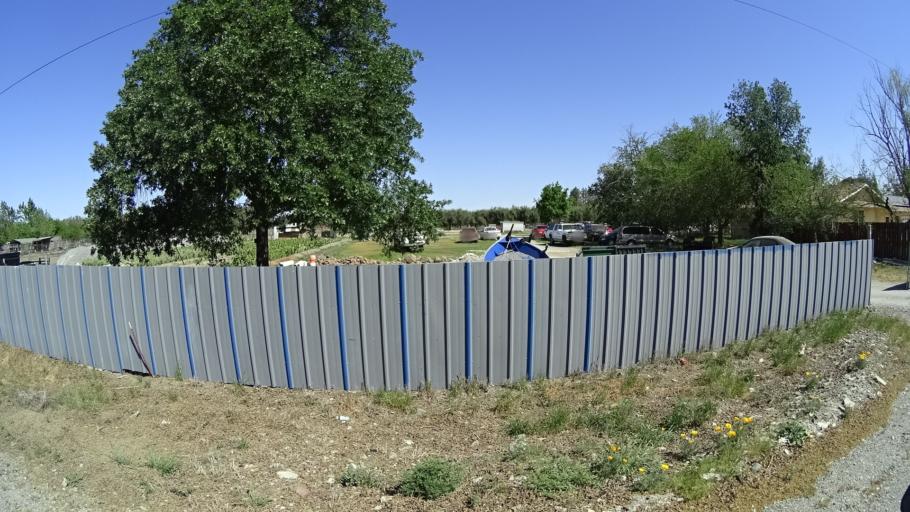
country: US
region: California
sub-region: Glenn County
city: Orland
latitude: 39.7584
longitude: -122.2034
